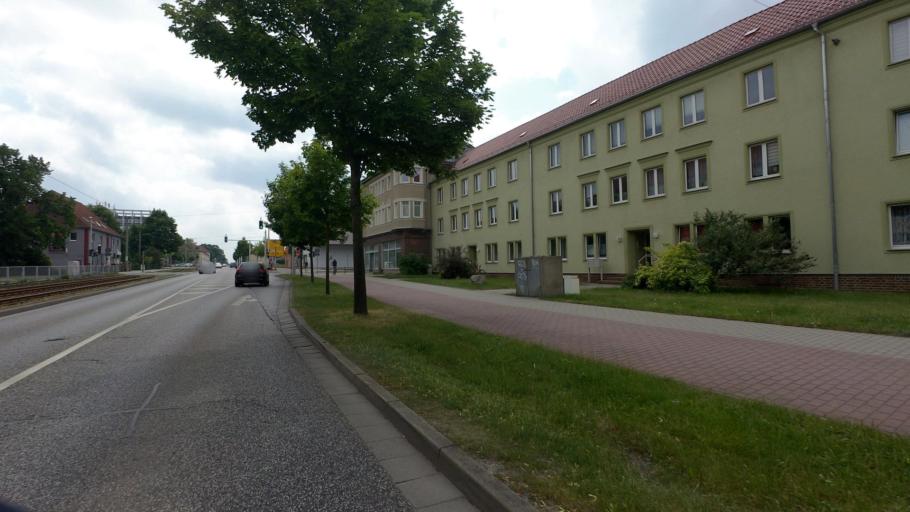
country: DE
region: Brandenburg
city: Cottbus
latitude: 51.7419
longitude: 14.3333
